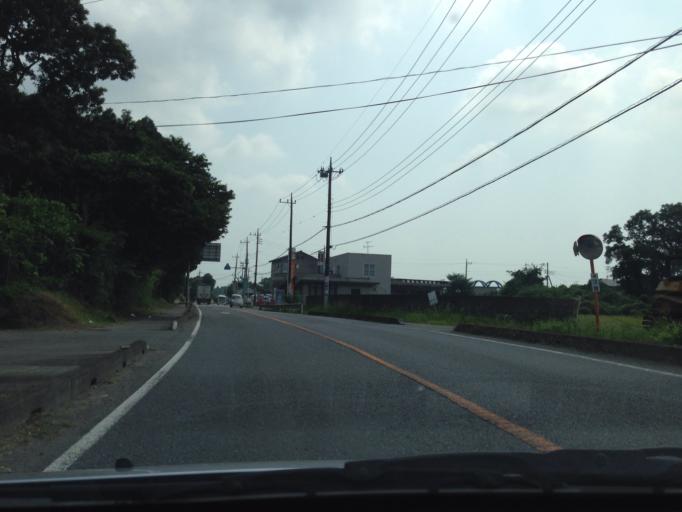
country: JP
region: Ibaraki
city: Inashiki
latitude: 36.0034
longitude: 140.3091
